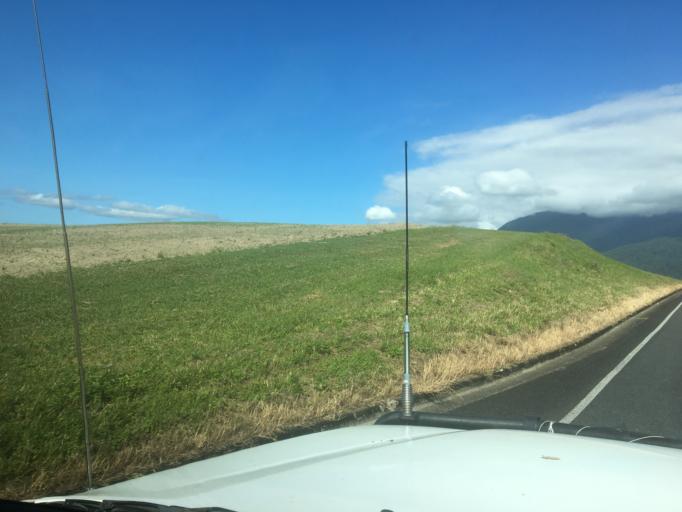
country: AU
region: Queensland
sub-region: Cassowary Coast
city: Innisfail
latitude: -17.3477
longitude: 145.9042
